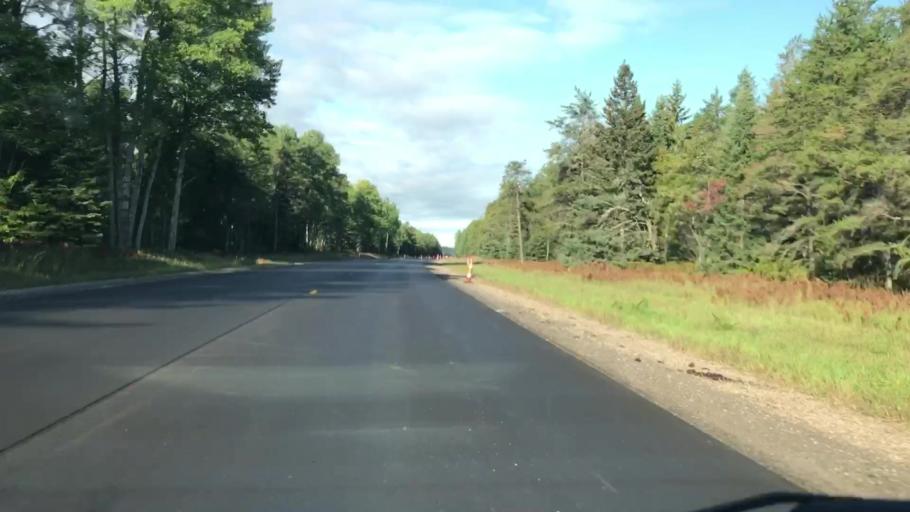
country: US
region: Michigan
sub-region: Mackinac County
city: Saint Ignace
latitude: 46.3459
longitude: -84.9248
